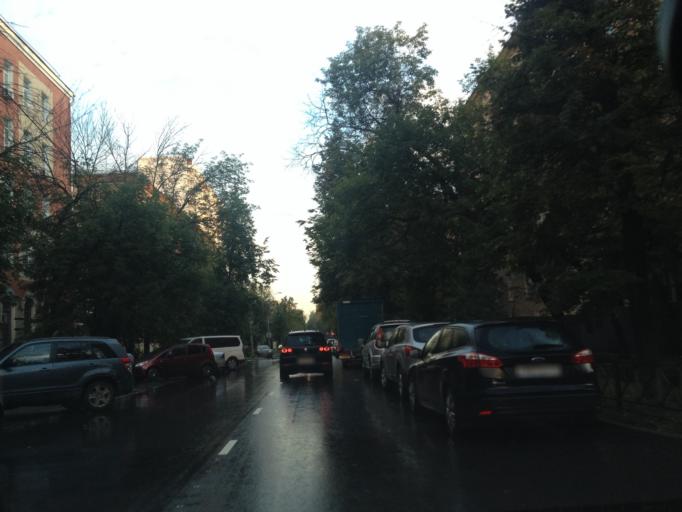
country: RU
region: Moscow
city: Metrogorodok
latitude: 55.8008
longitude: 37.7936
